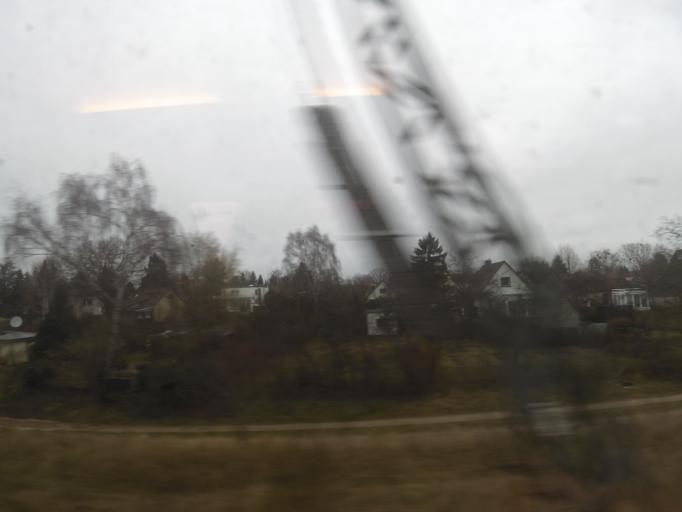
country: DE
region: Berlin
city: Falkenhagener Feld
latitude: 52.5403
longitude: 13.1645
